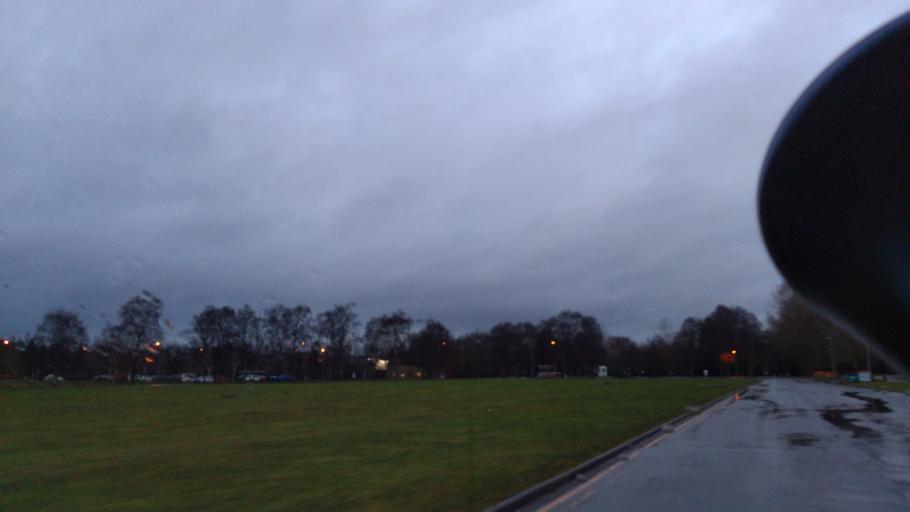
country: GB
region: England
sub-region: Oxfordshire
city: Shrivenham
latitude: 51.6119
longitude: -1.6351
